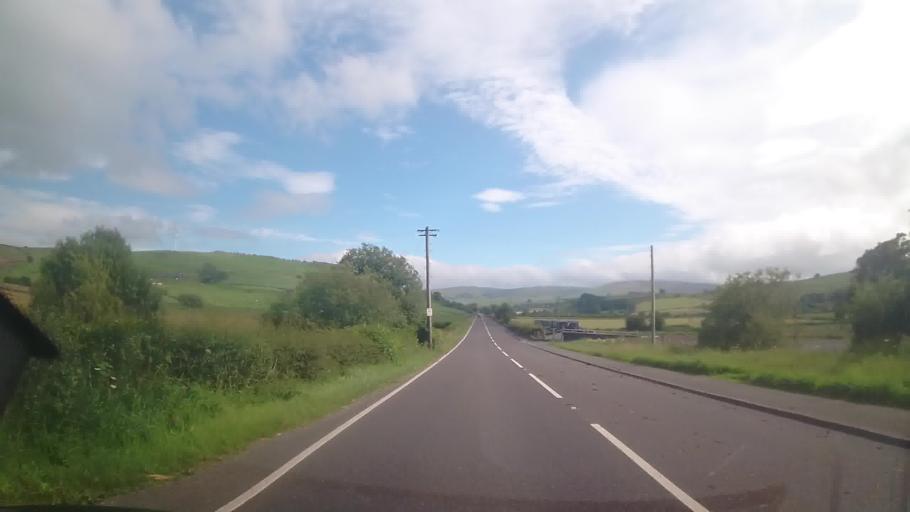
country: GB
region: Wales
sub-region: Conwy
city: Llangwm
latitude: 53.0210
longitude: -3.5590
